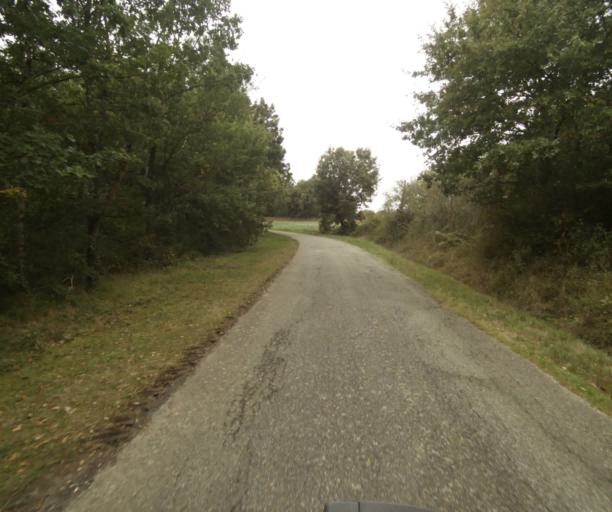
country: FR
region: Midi-Pyrenees
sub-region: Departement du Tarn-et-Garonne
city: Beaumont-de-Lomagne
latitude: 43.8437
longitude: 1.0978
